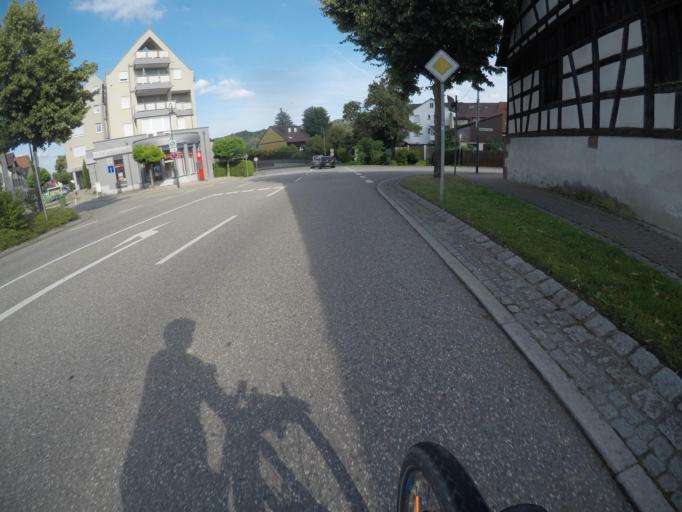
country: DE
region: Baden-Wuerttemberg
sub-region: Karlsruhe Region
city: Niefern-Oschelbronn
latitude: 48.9347
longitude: 8.7990
